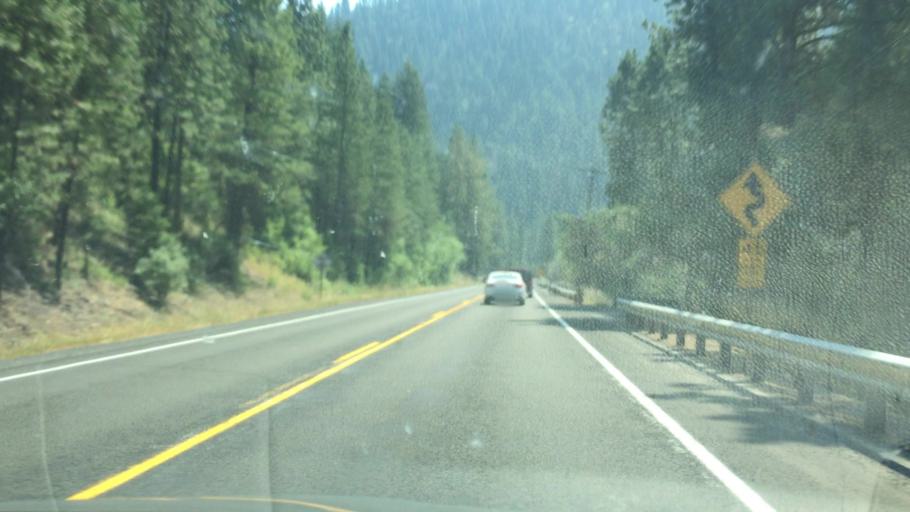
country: US
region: Idaho
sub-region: Valley County
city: McCall
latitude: 45.1519
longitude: -116.2969
